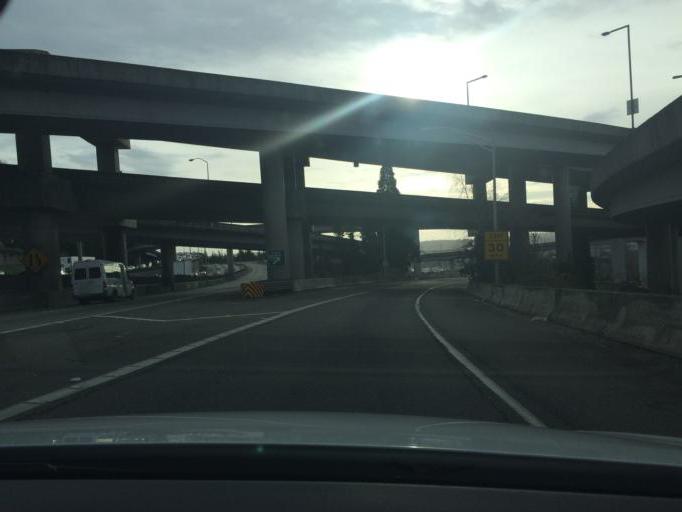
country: US
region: Washington
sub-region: King County
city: Seattle
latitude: 47.5944
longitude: -122.3211
